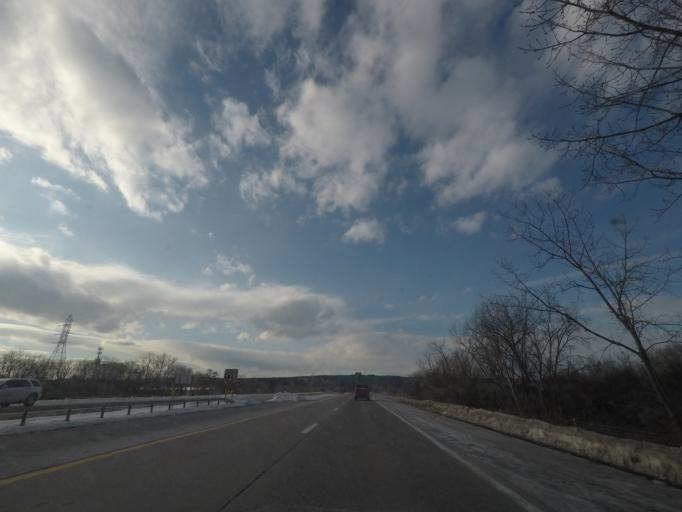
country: US
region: New York
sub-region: Schenectady County
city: Scotia
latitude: 42.8136
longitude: -73.9745
